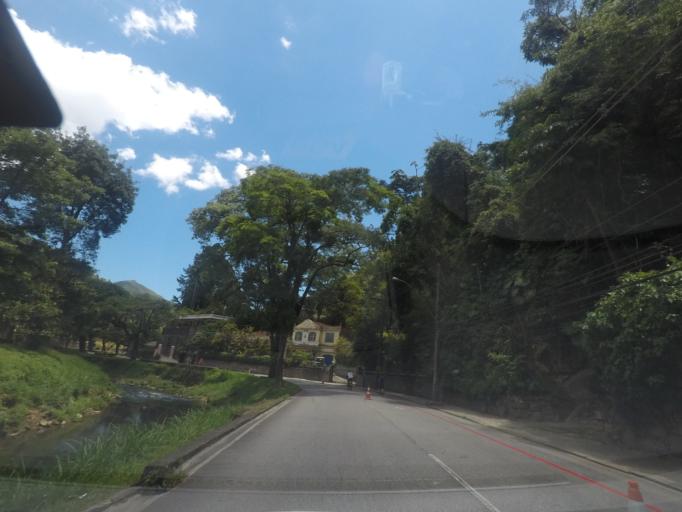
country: BR
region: Rio de Janeiro
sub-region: Petropolis
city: Petropolis
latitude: -22.4990
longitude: -43.1804
